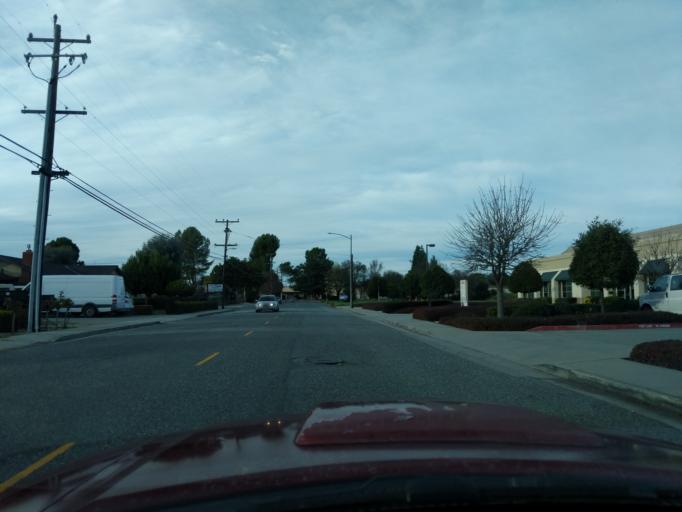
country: US
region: California
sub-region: Santa Clara County
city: Morgan Hill
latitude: 37.1172
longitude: -121.6428
